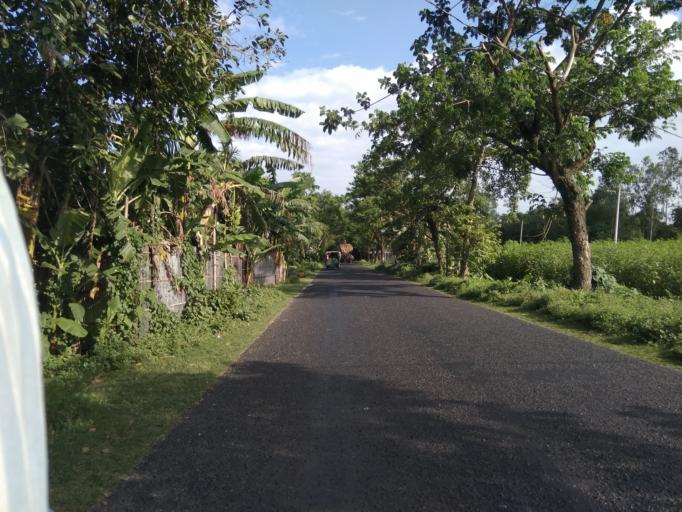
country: BD
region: Rangpur Division
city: Rangpur
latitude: 25.8420
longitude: 89.1131
